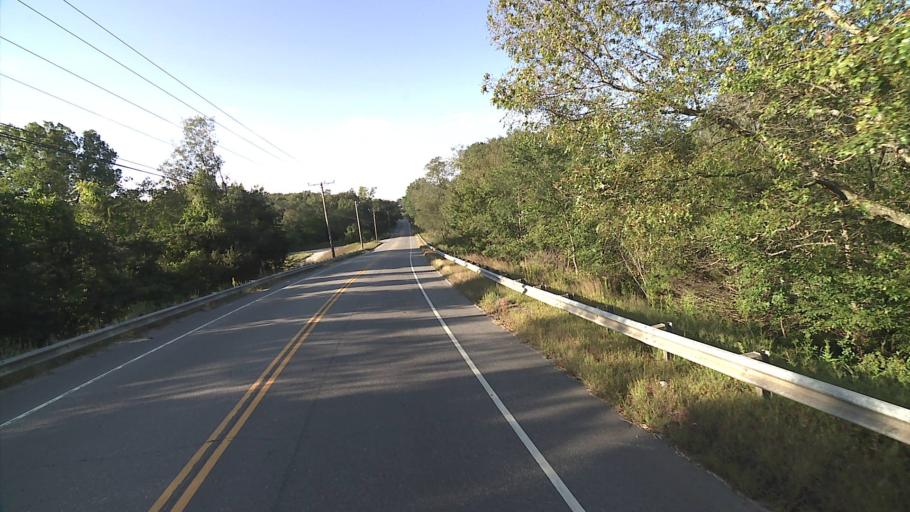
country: US
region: Connecticut
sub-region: Windham County
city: South Windham
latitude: 41.6547
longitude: -72.1584
